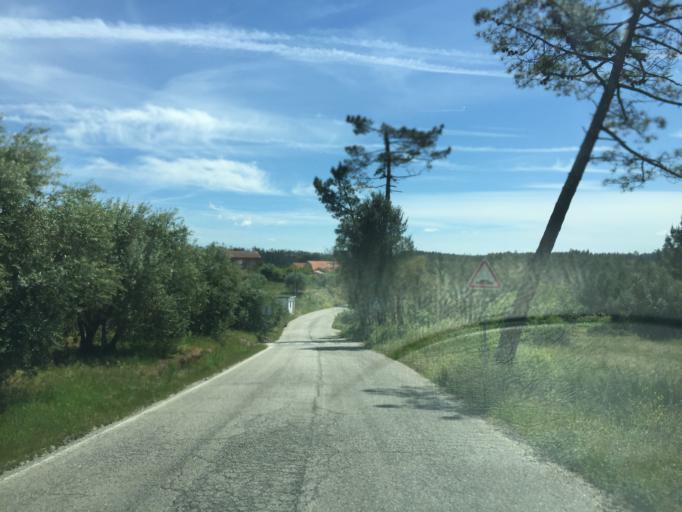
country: PT
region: Coimbra
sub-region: Soure
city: Soure
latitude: 40.0529
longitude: -8.6748
